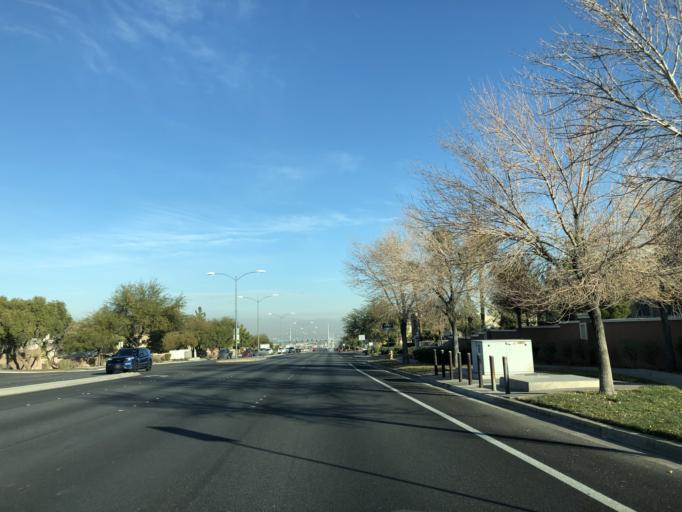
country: US
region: Nevada
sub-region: Clark County
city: Whitney
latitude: 36.0230
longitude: -115.0472
